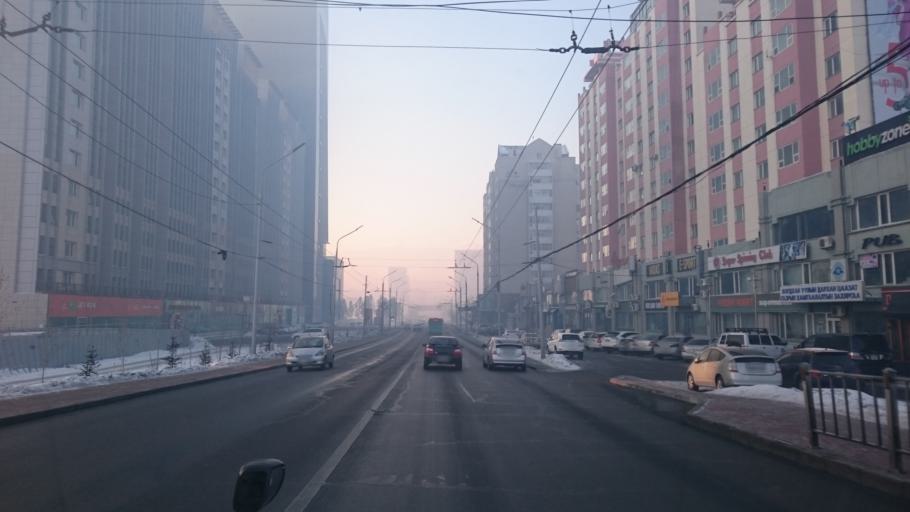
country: MN
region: Ulaanbaatar
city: Ulaanbaatar
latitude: 47.9058
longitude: 106.9121
